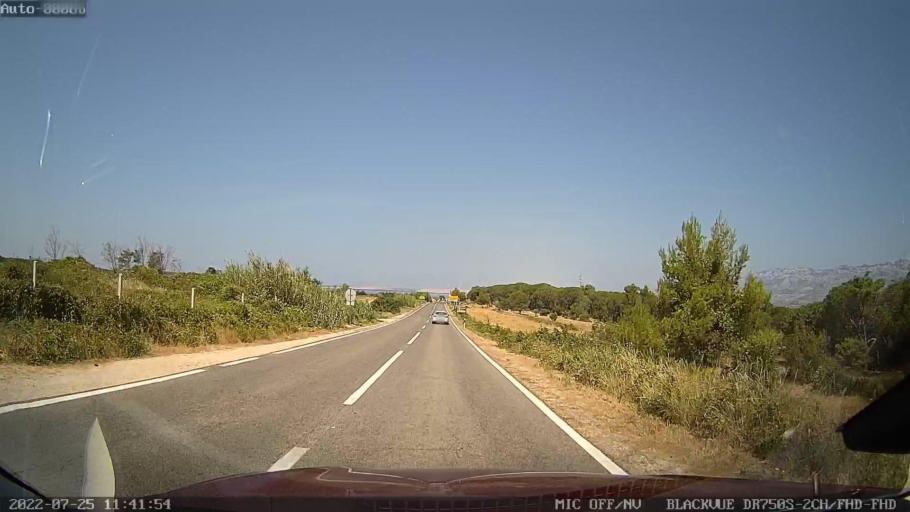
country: HR
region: Zadarska
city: Razanac
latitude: 44.2705
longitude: 15.3424
